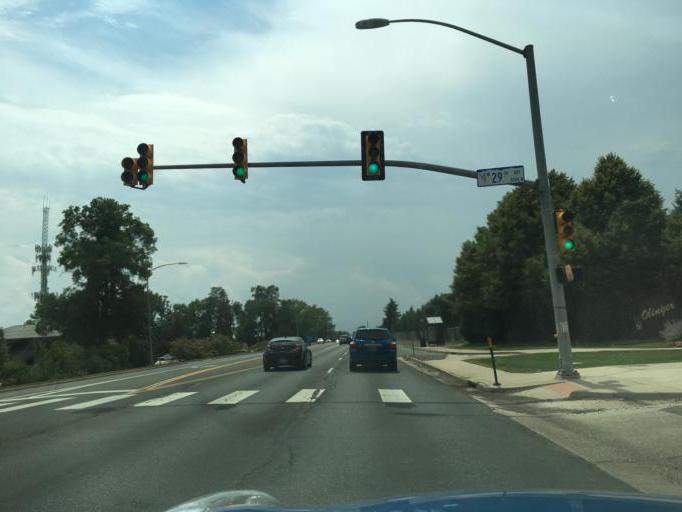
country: US
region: Colorado
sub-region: Jefferson County
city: Wheat Ridge
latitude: 39.7587
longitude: -105.0816
